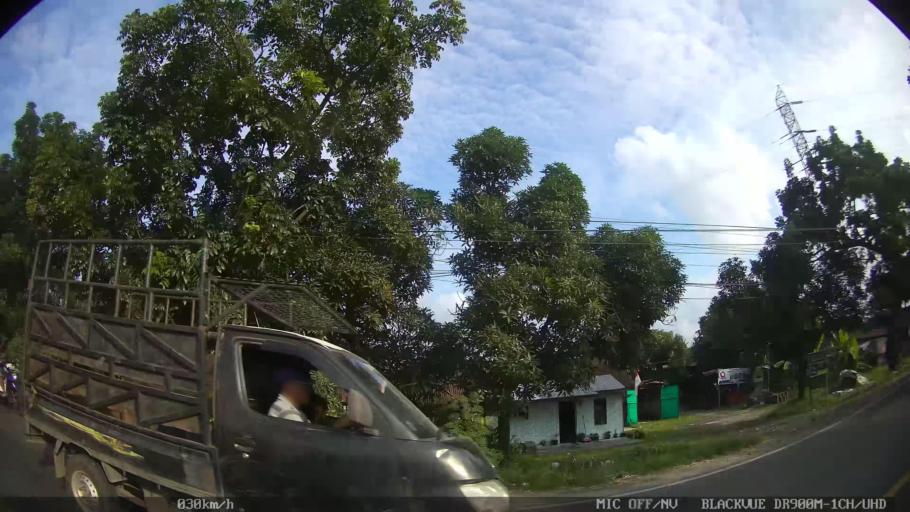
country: ID
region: North Sumatra
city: Medan
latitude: 3.6179
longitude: 98.6546
